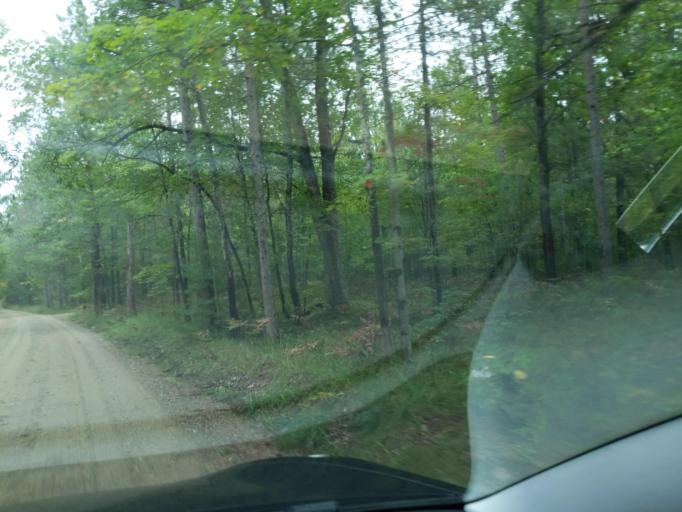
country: US
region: Michigan
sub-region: Grand Traverse County
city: Kingsley
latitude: 44.6943
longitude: -85.4117
